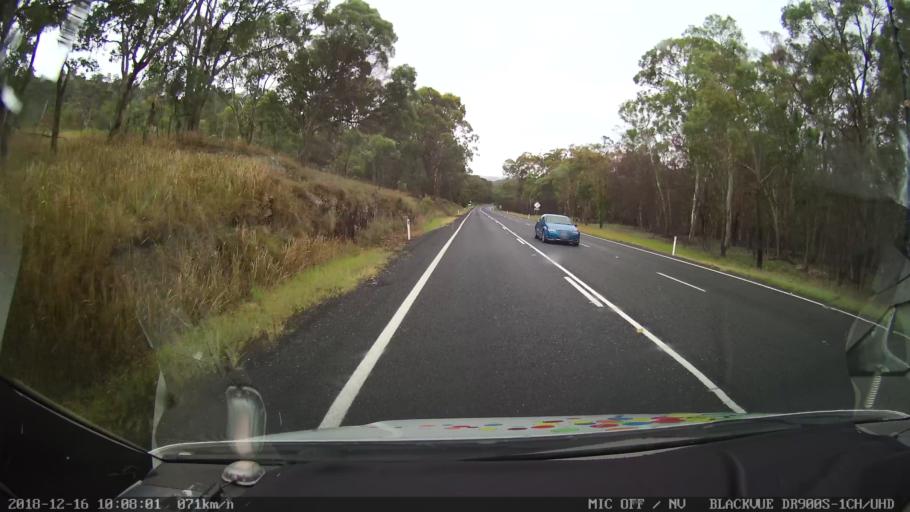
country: AU
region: New South Wales
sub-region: Glen Innes Severn
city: Glen Innes
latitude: -29.3323
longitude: 151.9013
